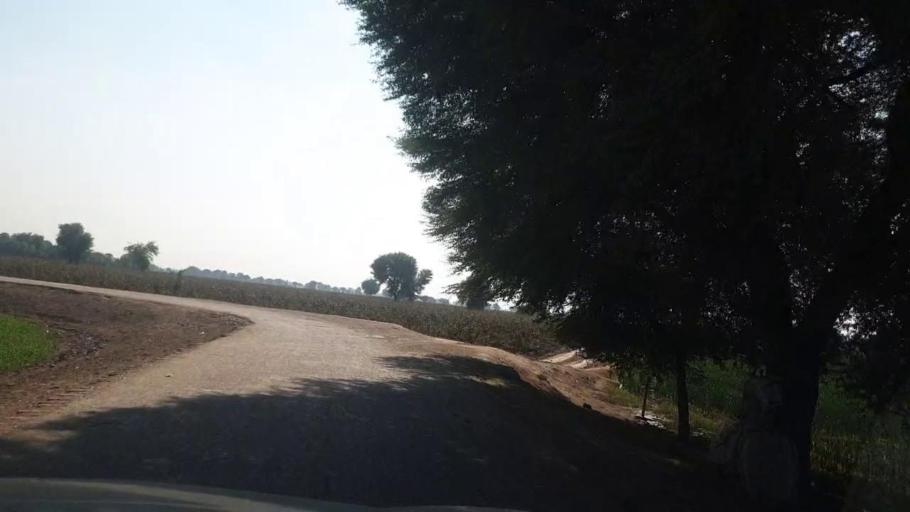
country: PK
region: Sindh
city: Bhan
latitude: 26.5791
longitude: 67.6943
